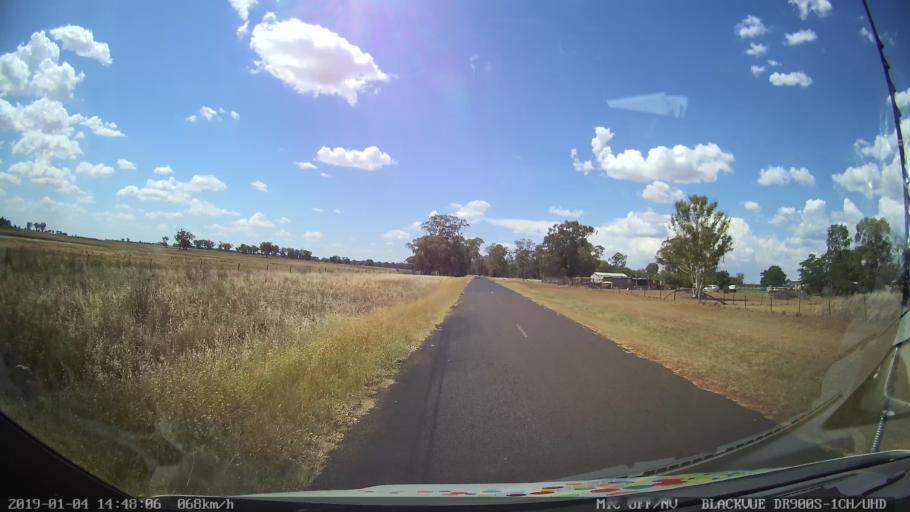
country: AU
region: New South Wales
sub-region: Dubbo Municipality
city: Dubbo
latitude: -32.0626
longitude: 148.6626
